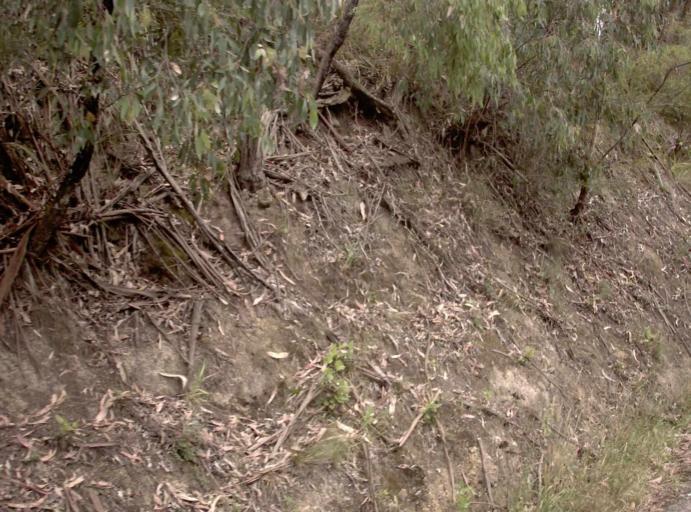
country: AU
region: Victoria
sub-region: Latrobe
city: Moe
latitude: -37.9846
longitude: 146.1439
